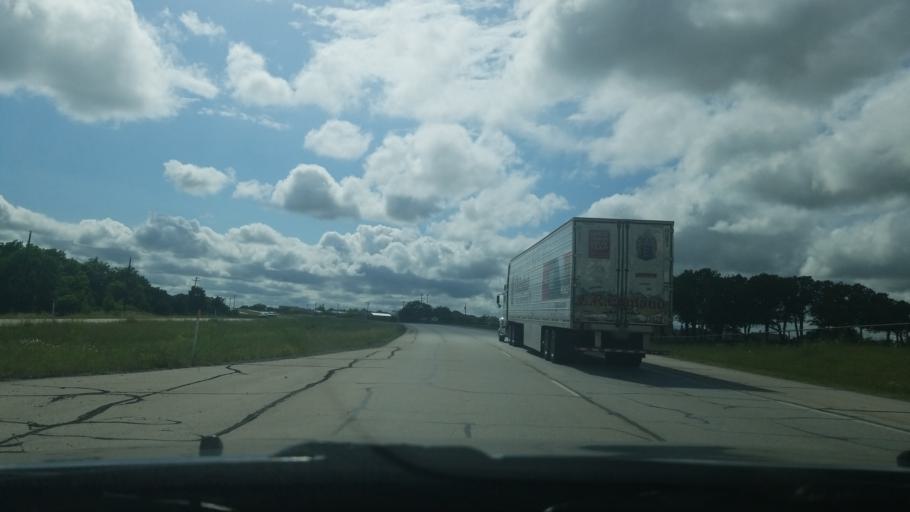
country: US
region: Texas
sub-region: Denton County
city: Ponder
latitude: 33.2507
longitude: -97.4103
